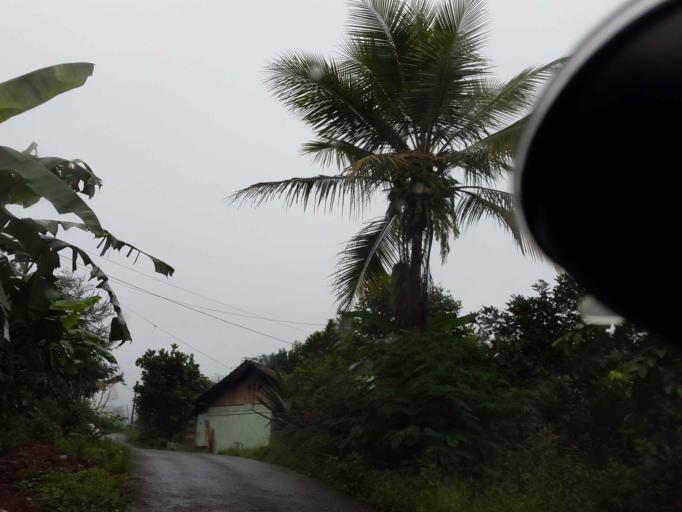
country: ID
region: Central Java
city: Wonosobo
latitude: -7.4681
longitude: 109.9395
